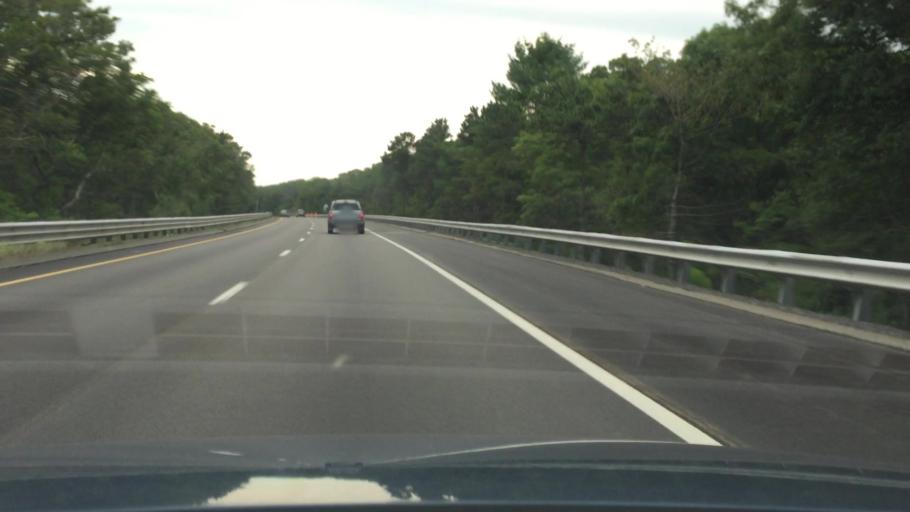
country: US
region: Massachusetts
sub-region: Plymouth County
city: Plymouth
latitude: 41.9309
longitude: -70.6377
